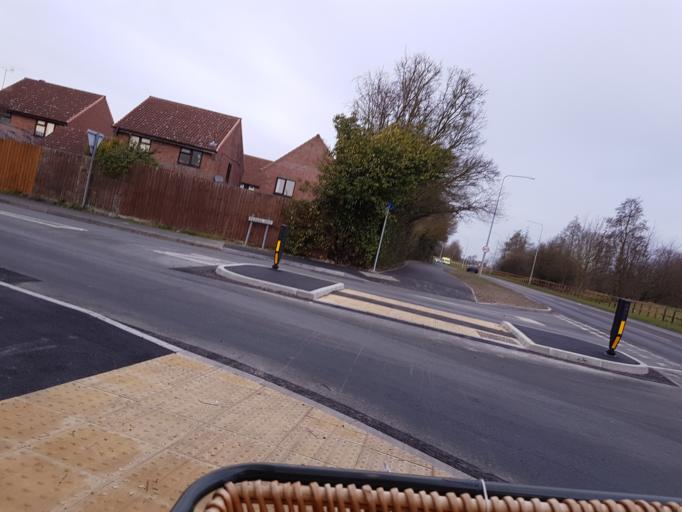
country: GB
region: England
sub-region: Cambridgeshire
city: Fulbourn
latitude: 52.1840
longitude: 0.1847
